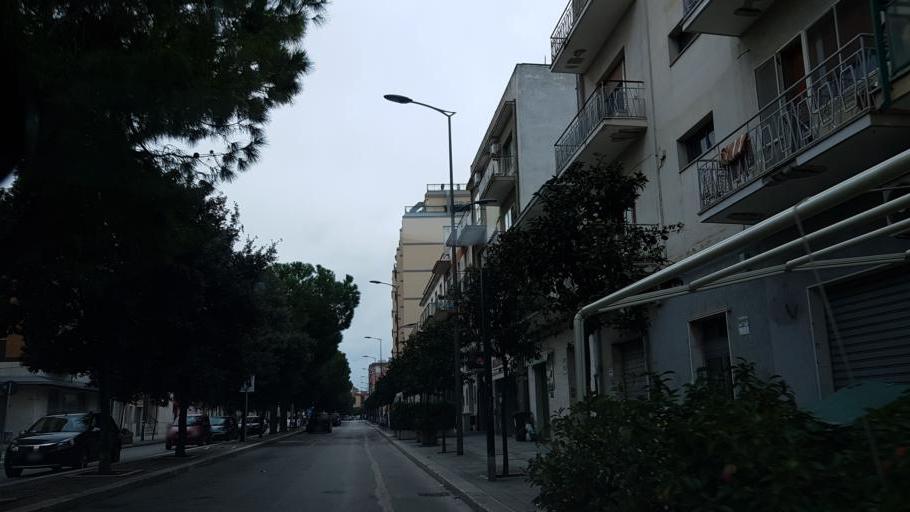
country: IT
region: Apulia
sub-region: Provincia di Brindisi
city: Brindisi
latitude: 40.6312
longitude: 17.9359
